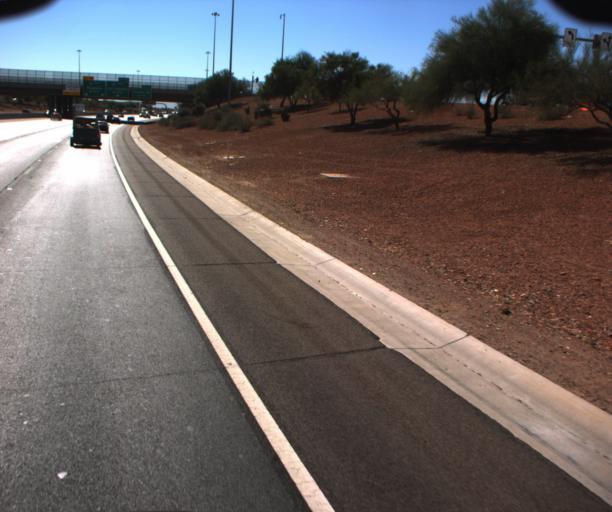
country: US
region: Arizona
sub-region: Maricopa County
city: Tolleson
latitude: 33.4955
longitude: -112.2645
